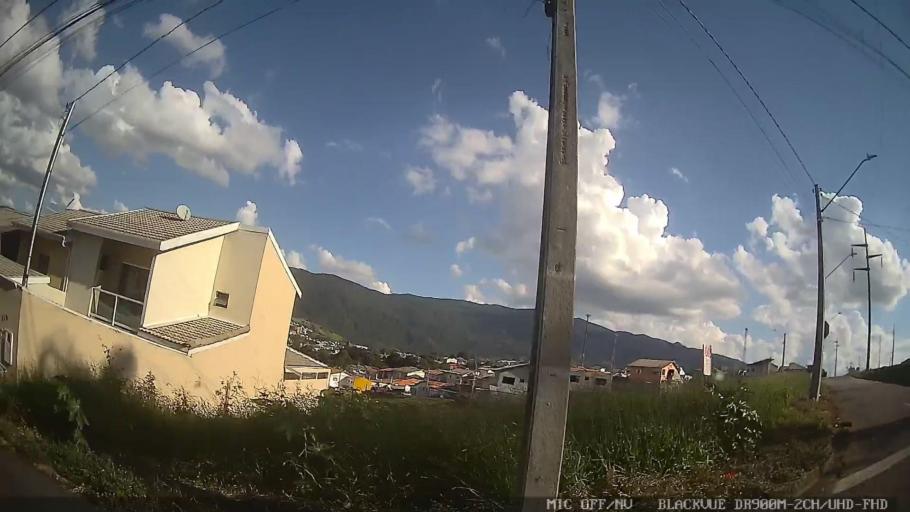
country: BR
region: Minas Gerais
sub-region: Extrema
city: Extrema
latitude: -22.8430
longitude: -46.3283
